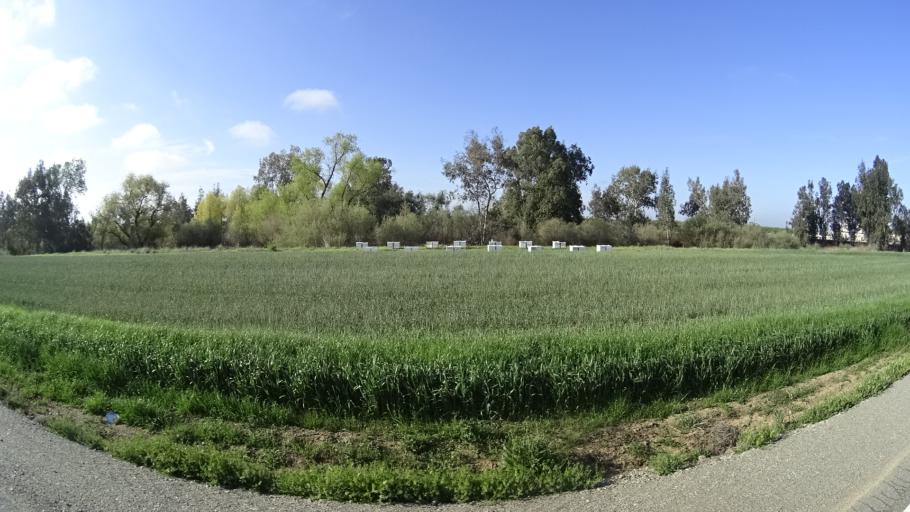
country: US
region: California
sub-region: Glenn County
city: Willows
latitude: 39.5840
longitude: -122.1886
